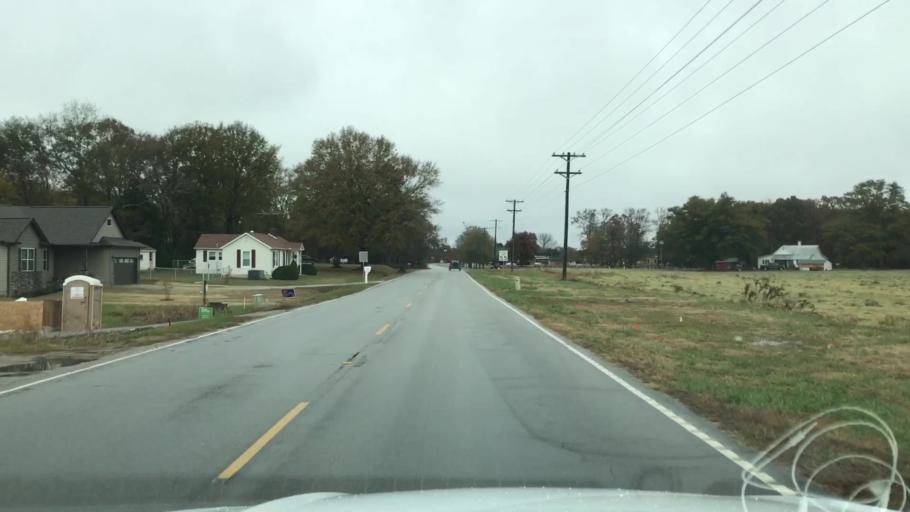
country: US
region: South Carolina
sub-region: Spartanburg County
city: Roebuck
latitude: 34.7997
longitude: -81.9160
